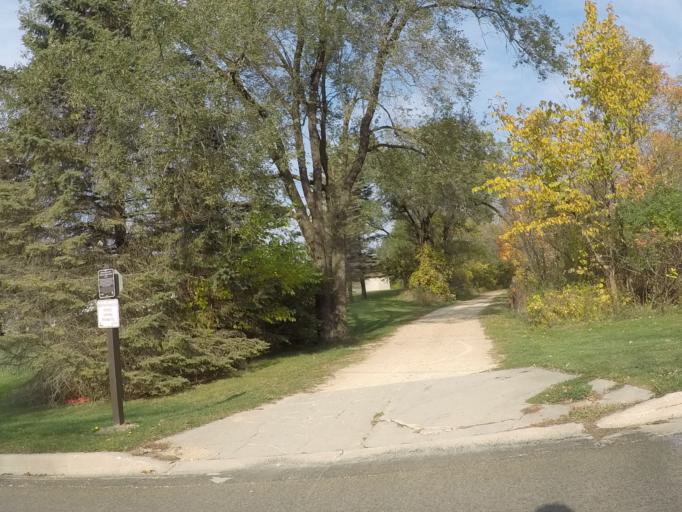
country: US
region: Wisconsin
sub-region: Iowa County
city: Barneveld
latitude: 43.0173
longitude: -89.8297
